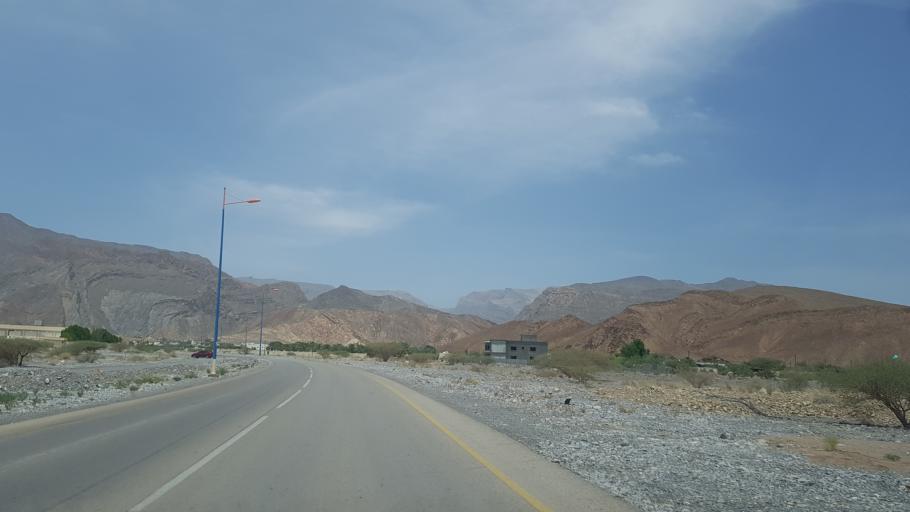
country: OM
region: Muhafazat ad Dakhiliyah
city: Izki
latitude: 22.9073
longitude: 57.6768
